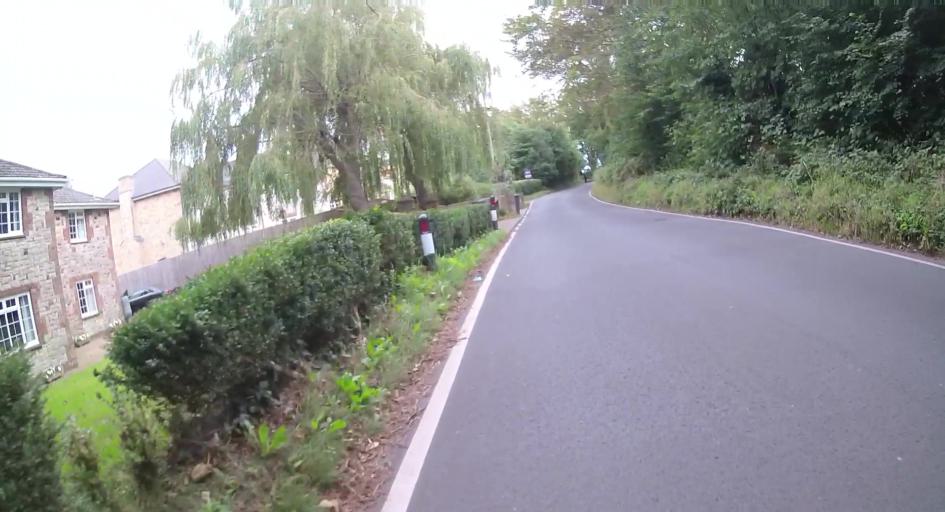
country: GB
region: England
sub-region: Isle of Wight
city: Totland
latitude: 50.6757
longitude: -1.5214
